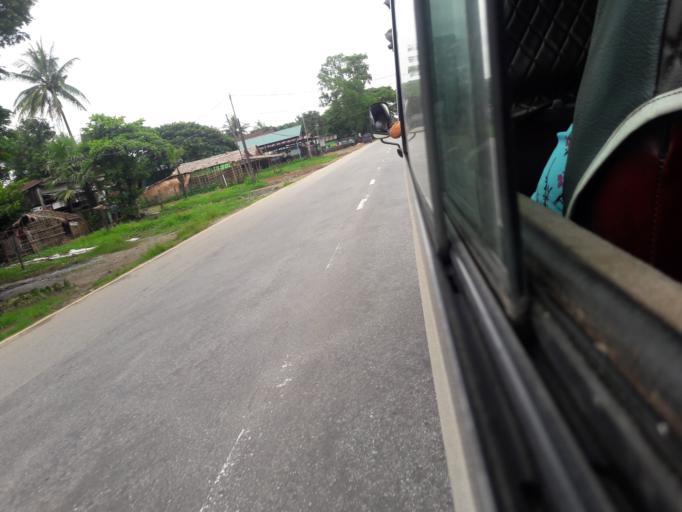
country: MM
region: Bago
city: Nyaunglebin
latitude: 17.8306
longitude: 96.6770
